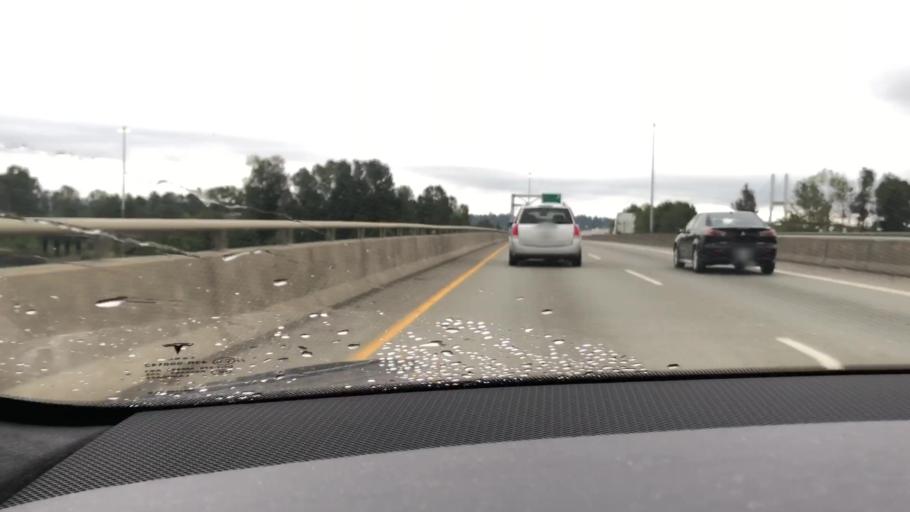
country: CA
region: British Columbia
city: New Westminster
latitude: 49.1751
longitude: -122.9596
